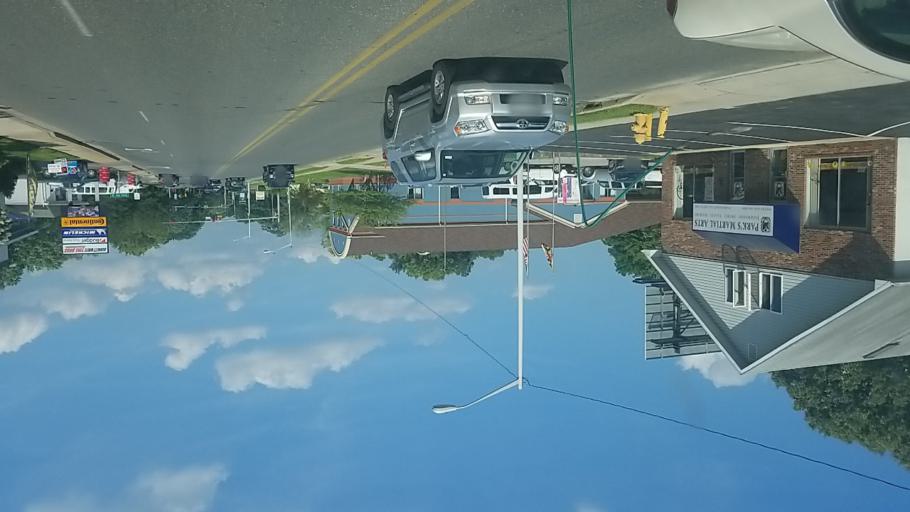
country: US
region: Maryland
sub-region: Wicomico County
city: Salisbury
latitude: 38.3657
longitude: -75.5942
